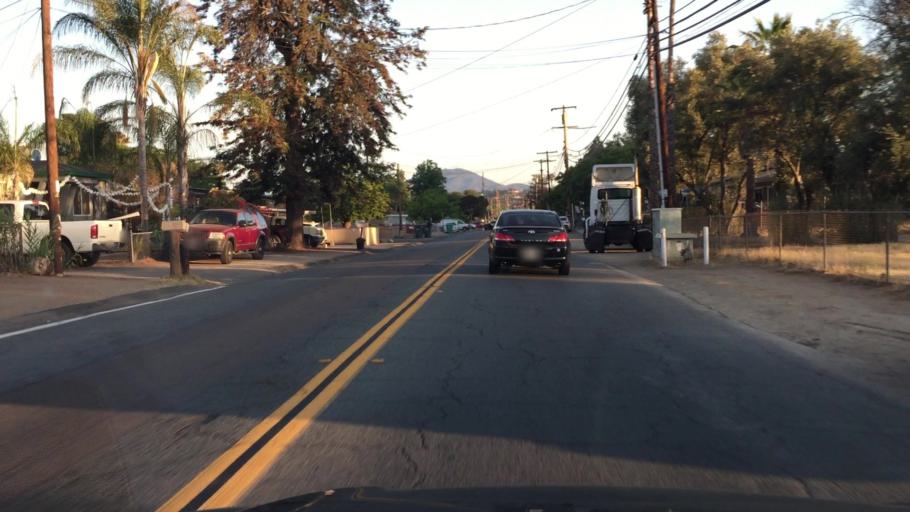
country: US
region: California
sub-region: San Diego County
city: Bostonia
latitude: 32.8112
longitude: -116.9446
